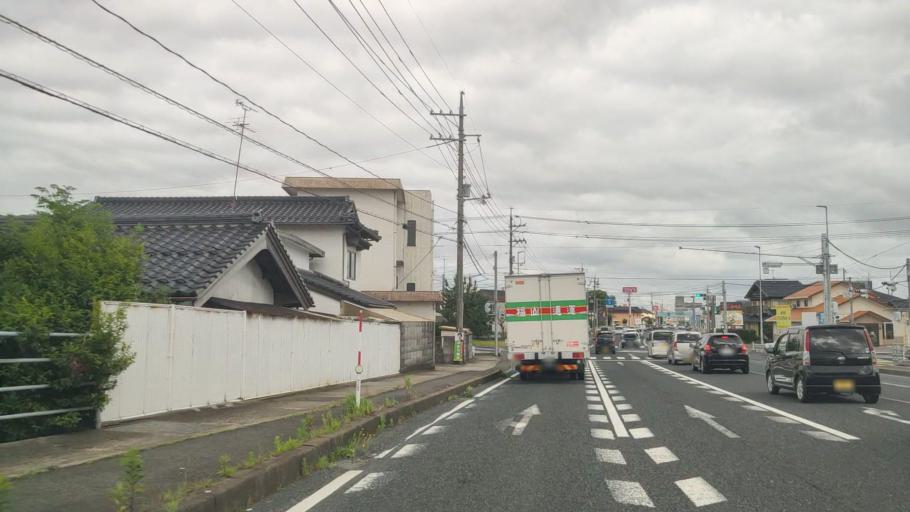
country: JP
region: Tottori
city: Yonago
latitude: 35.4318
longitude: 133.3625
